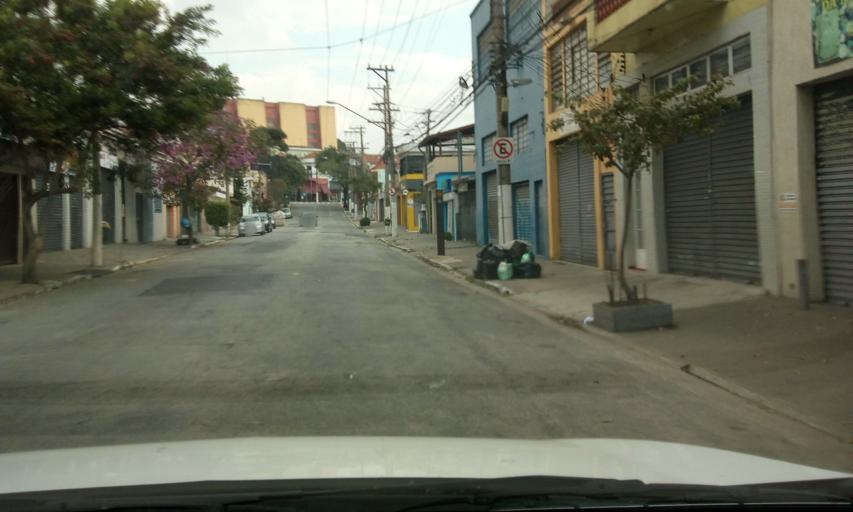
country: BR
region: Sao Paulo
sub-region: Sao Paulo
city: Sao Paulo
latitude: -23.5469
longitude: -46.5871
